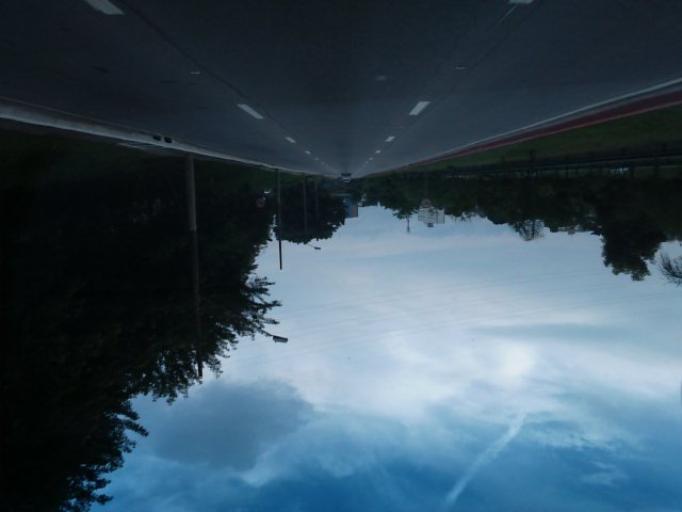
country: BR
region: Sao Paulo
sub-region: Sao Jose Dos Campos
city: Sao Jose dos Campos
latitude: -23.1912
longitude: -45.8827
